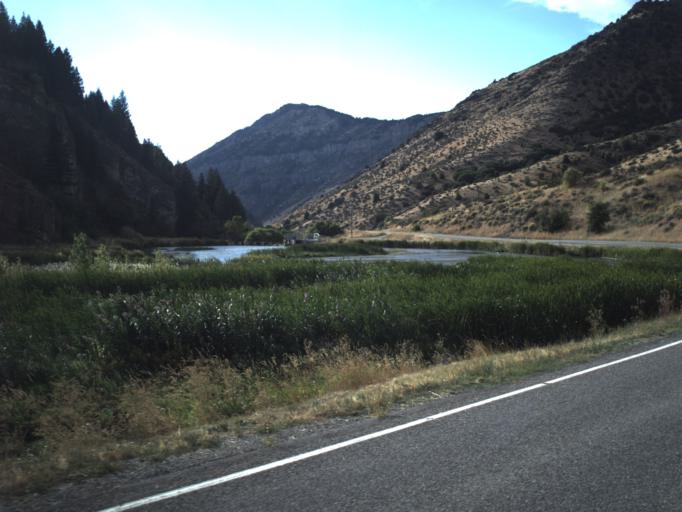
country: US
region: Utah
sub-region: Cache County
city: Millville
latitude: 41.6268
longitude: -111.6751
